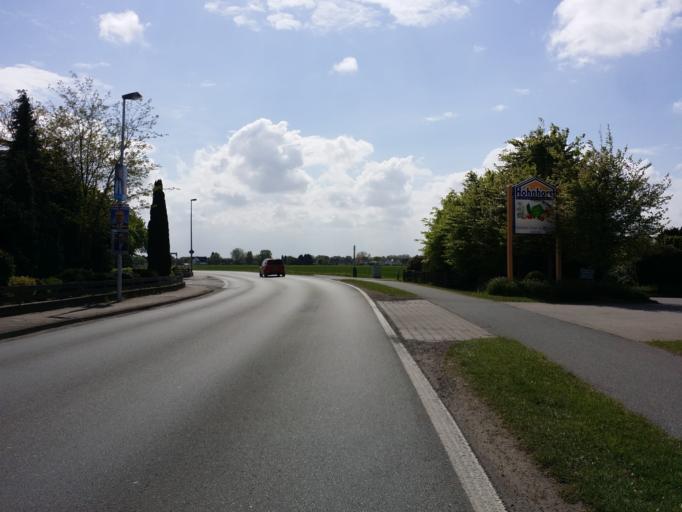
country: DE
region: Lower Saxony
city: Stuhr
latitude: 53.0247
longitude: 8.7442
